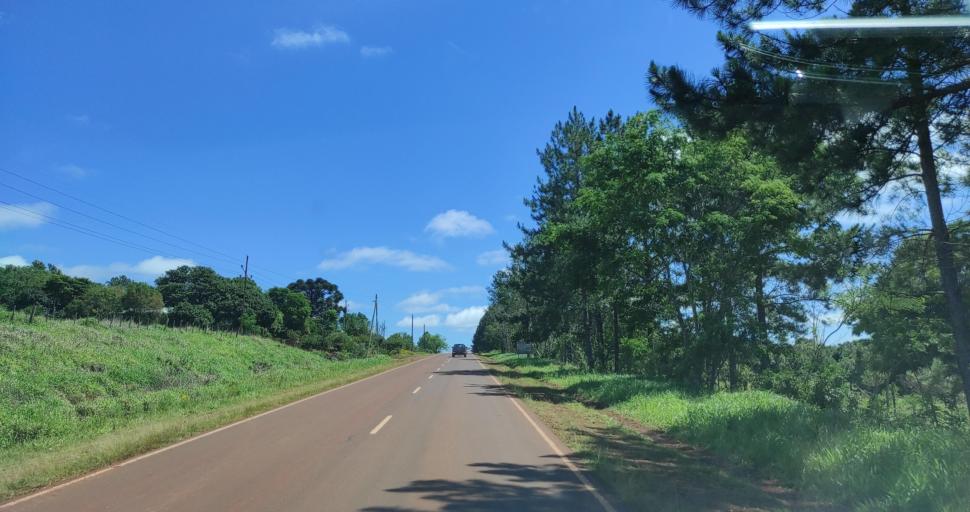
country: AR
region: Misiones
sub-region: Departamento de Veinticinco de Mayo
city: Veinticinco de Mayo
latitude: -27.3999
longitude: -54.7501
